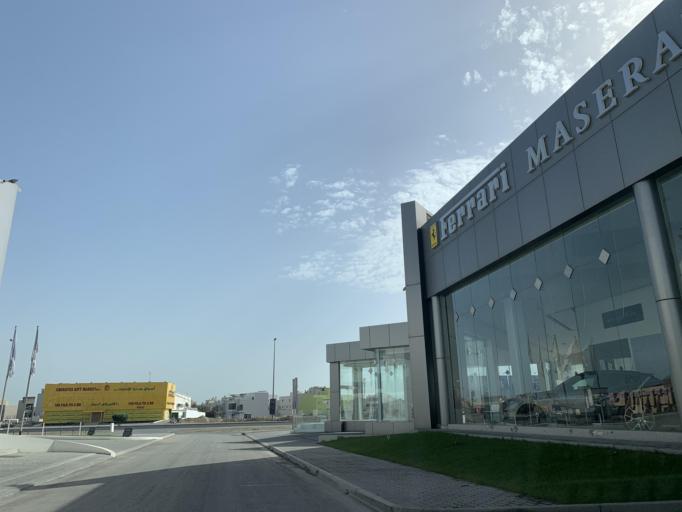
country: BH
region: Northern
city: Sitrah
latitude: 26.1536
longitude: 50.6117
